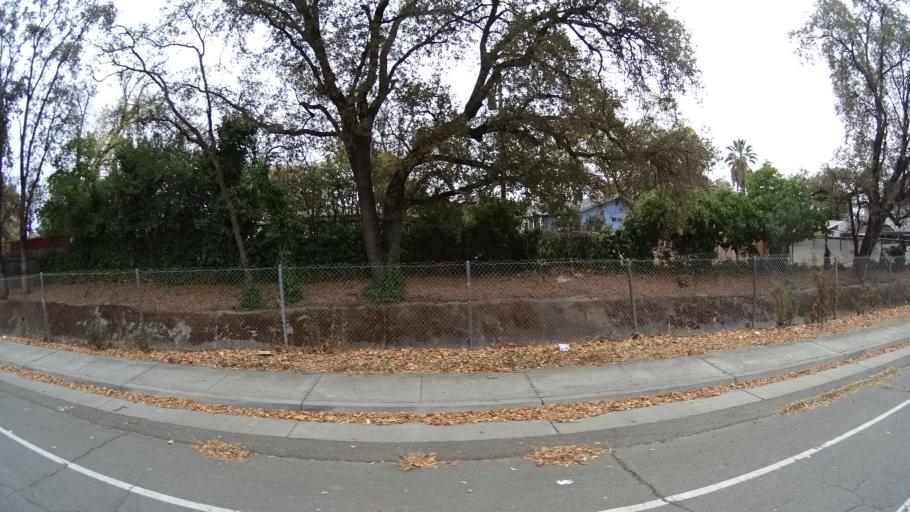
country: US
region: California
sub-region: Sacramento County
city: Citrus Heights
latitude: 38.7094
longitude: -121.3032
